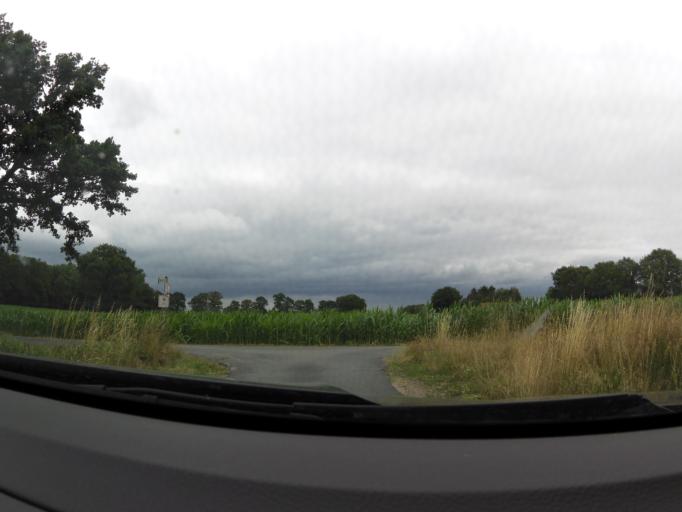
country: DE
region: North Rhine-Westphalia
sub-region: Regierungsbezirk Dusseldorf
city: Kevelaer
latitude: 51.5565
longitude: 6.2261
